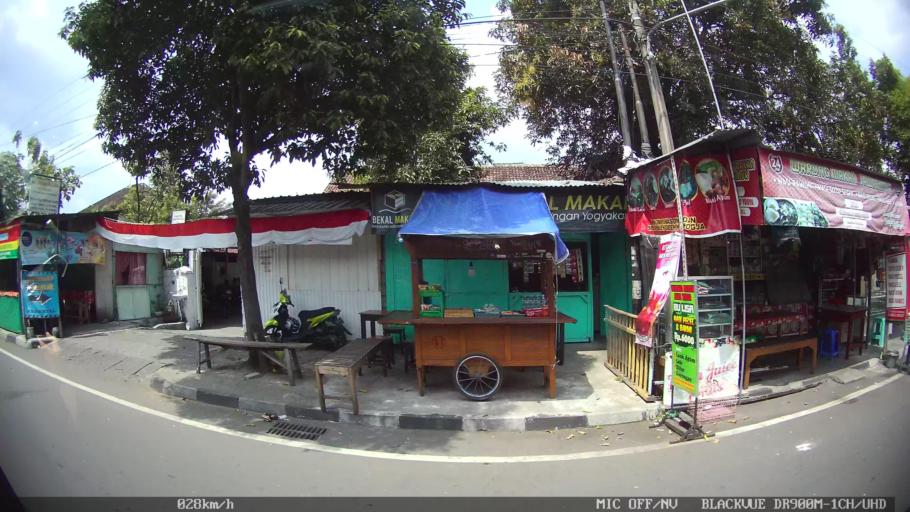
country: ID
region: Daerah Istimewa Yogyakarta
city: Yogyakarta
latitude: -7.7904
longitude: 110.3763
